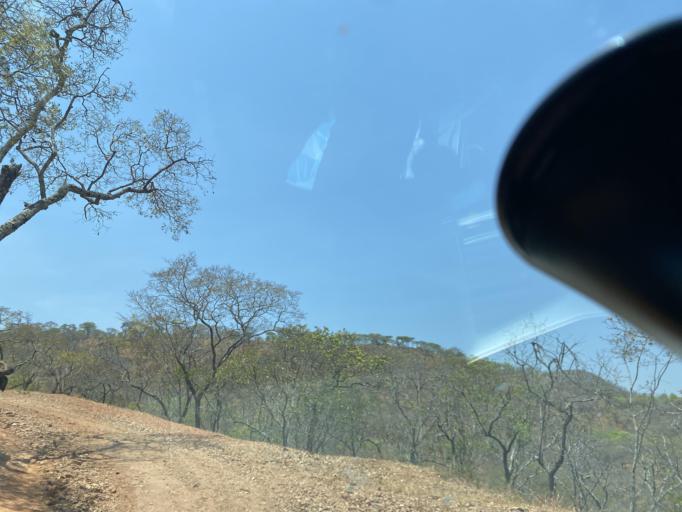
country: ZM
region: Lusaka
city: Kafue
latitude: -15.8082
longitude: 28.4384
